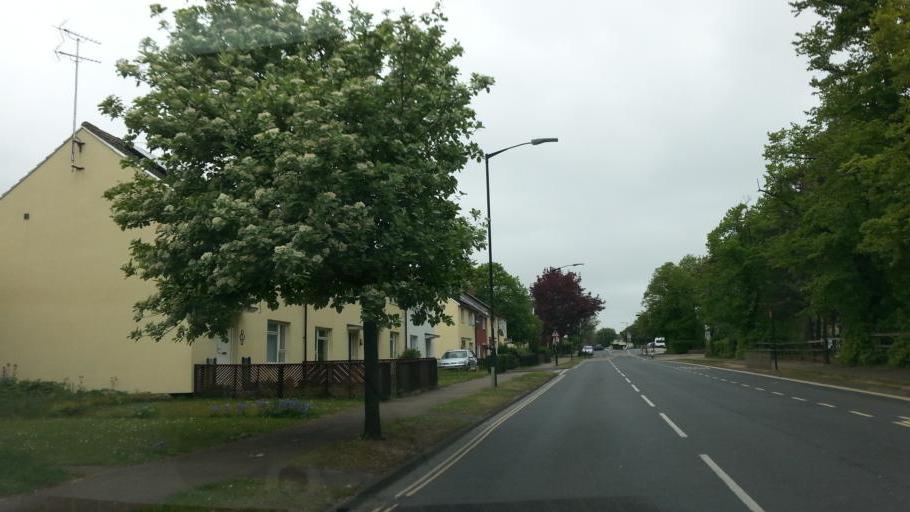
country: GB
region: England
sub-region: Suffolk
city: Bury St Edmunds
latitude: 52.2563
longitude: 0.7004
